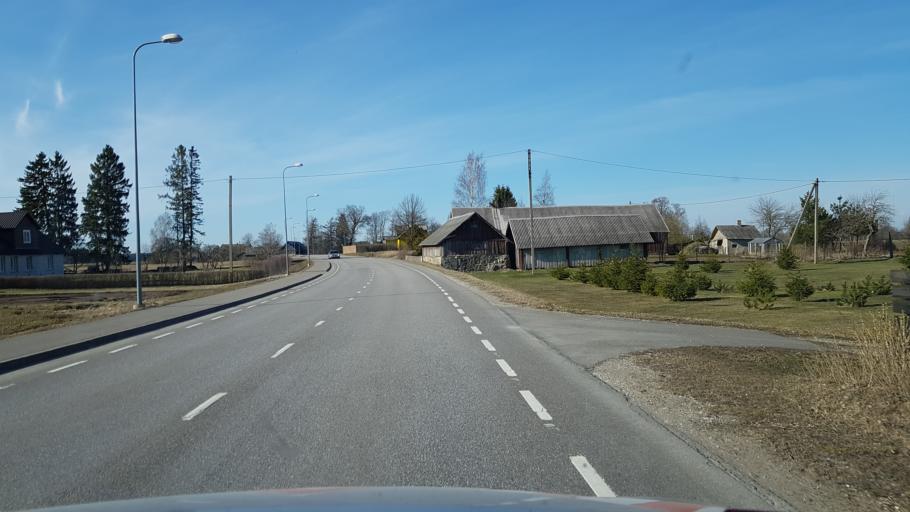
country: EE
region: Laeaene-Virumaa
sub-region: Vinni vald
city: Vinni
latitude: 59.1468
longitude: 26.5950
